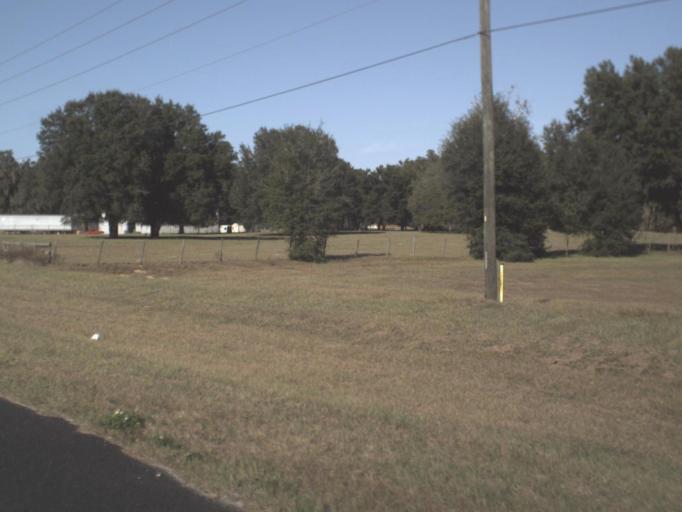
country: US
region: Florida
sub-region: Marion County
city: Belleview
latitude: 29.0260
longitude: -82.1008
